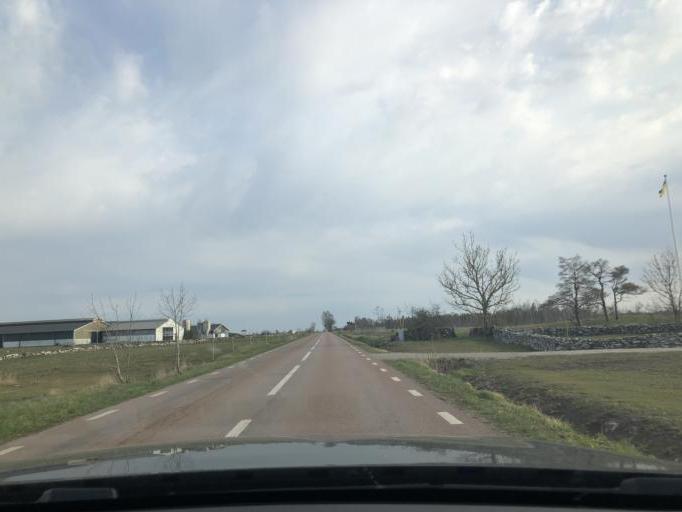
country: SE
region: Kalmar
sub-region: Morbylanga Kommun
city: Sodra Sandby
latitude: 56.5661
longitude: 16.6191
